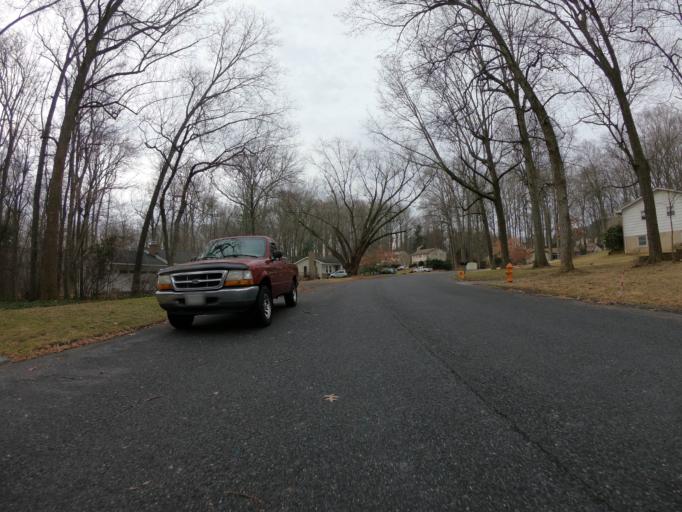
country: US
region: Maryland
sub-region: Howard County
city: Columbia
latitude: 39.2556
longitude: -76.8494
